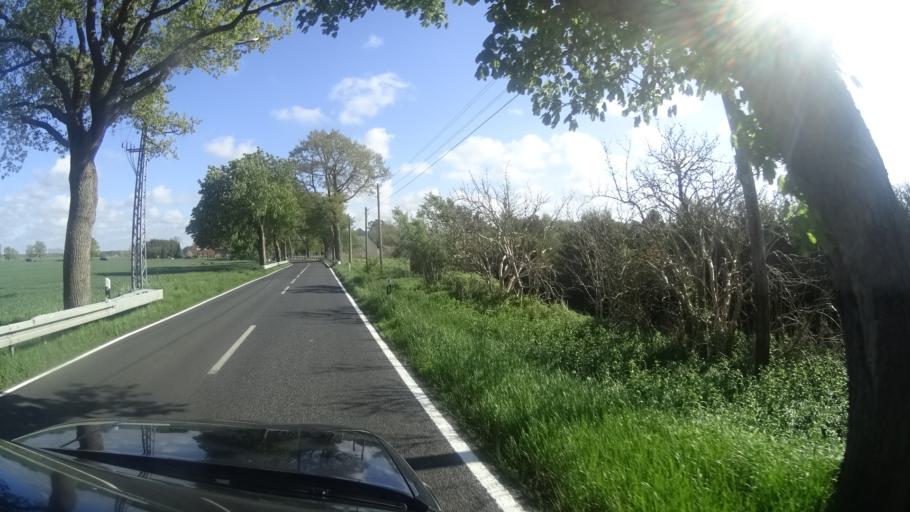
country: DE
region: Mecklenburg-Vorpommern
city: Gelbensande
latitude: 54.2392
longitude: 12.3202
